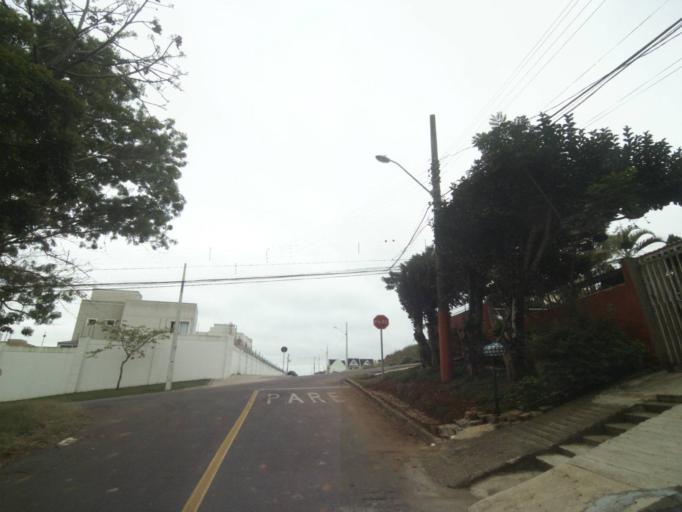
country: BR
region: Parana
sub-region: Sao Jose Dos Pinhais
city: Sao Jose dos Pinhais
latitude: -25.4813
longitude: -49.2345
